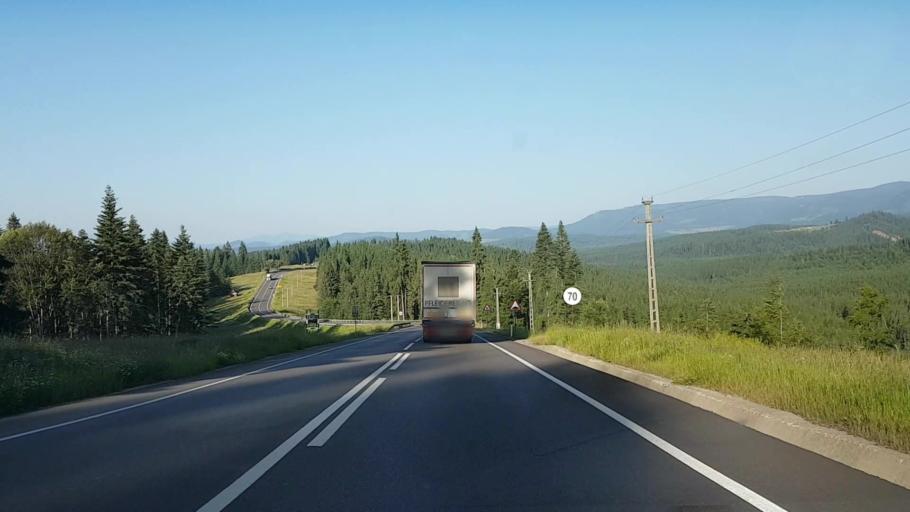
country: RO
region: Suceava
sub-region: Comuna Poiana Stampei
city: Poiana Stampei
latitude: 47.2842
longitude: 25.0510
